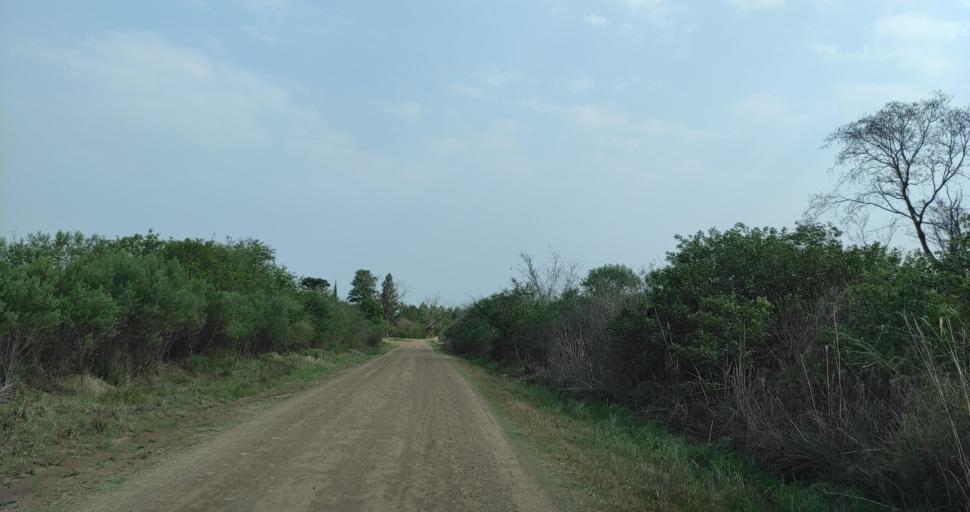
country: AR
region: Misiones
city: Cerro Cora
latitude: -27.5637
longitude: -55.5840
